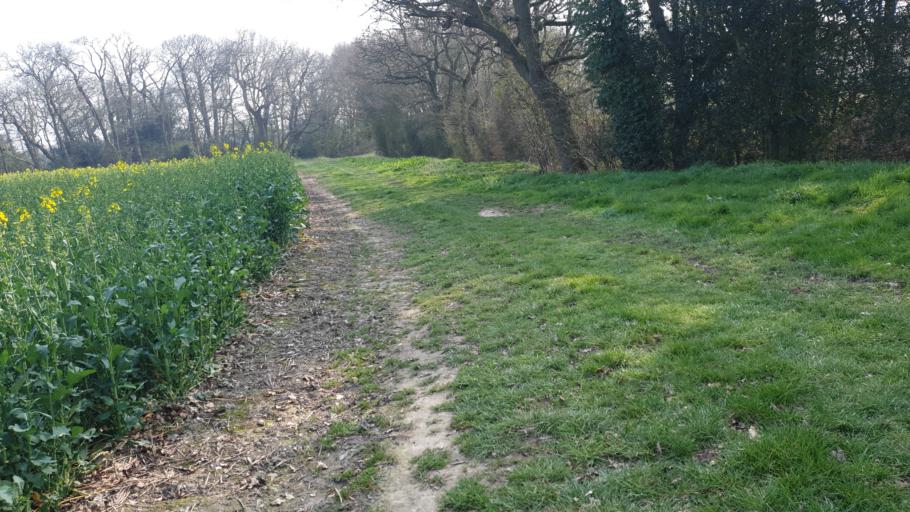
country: GB
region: England
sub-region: Essex
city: Great Bentley
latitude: 51.8859
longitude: 1.1191
